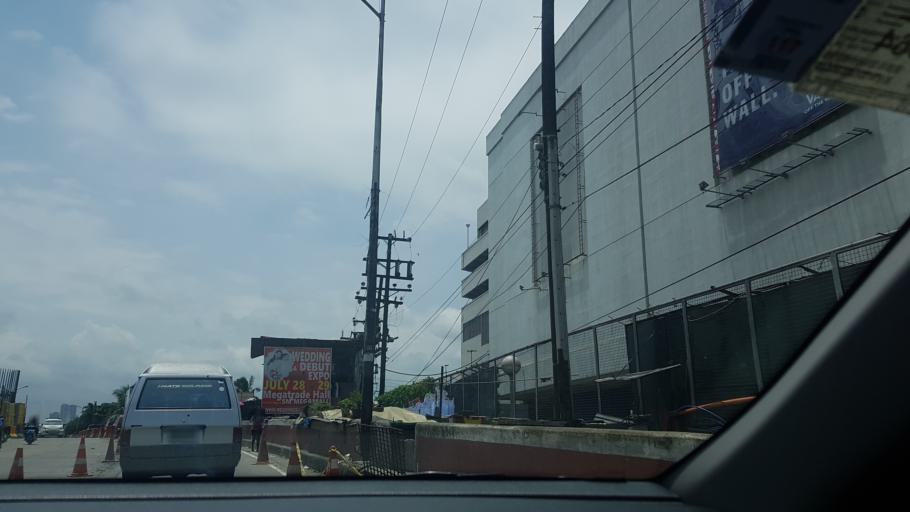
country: PH
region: Metro Manila
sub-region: San Juan
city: San Juan
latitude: 14.6049
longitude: 121.0193
